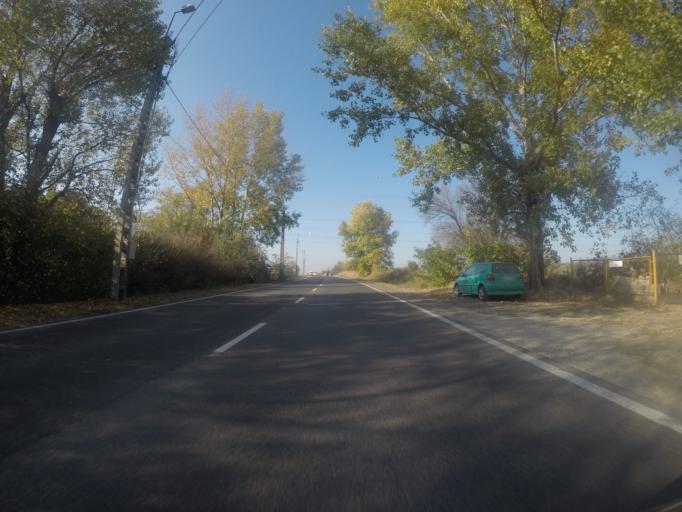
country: HU
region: Fejer
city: Ercsi
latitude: 47.2627
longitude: 18.8933
